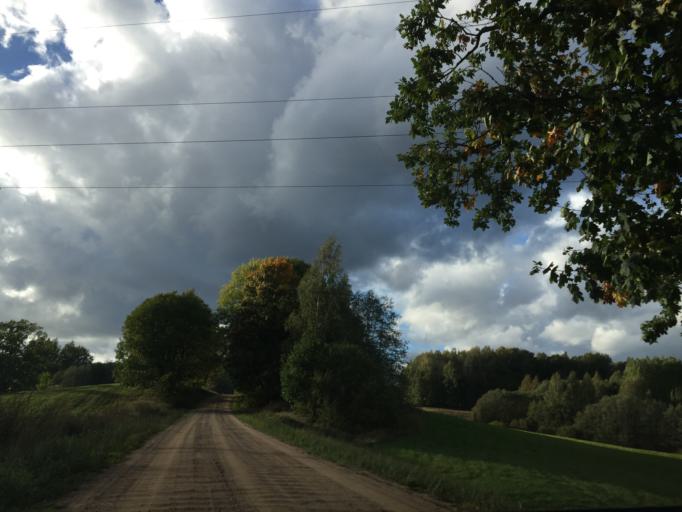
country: LV
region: Ligatne
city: Ligatne
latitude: 57.1369
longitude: 25.0891
